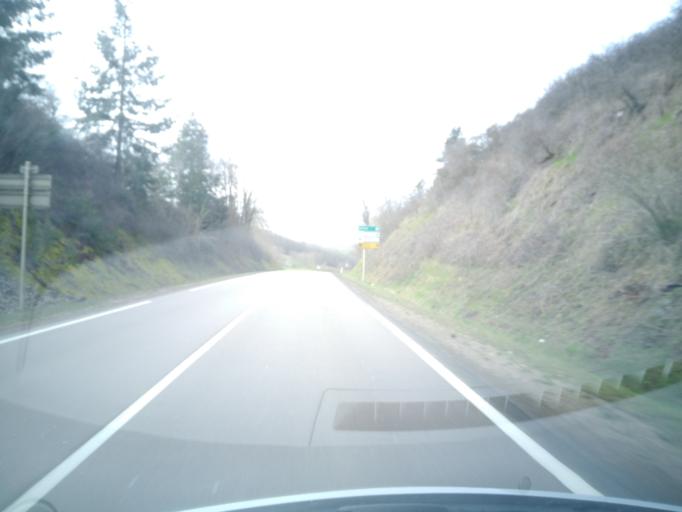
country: FR
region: Bourgogne
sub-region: Departement de Saone-et-Loire
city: Montcenis
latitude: 46.7983
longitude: 4.3884
